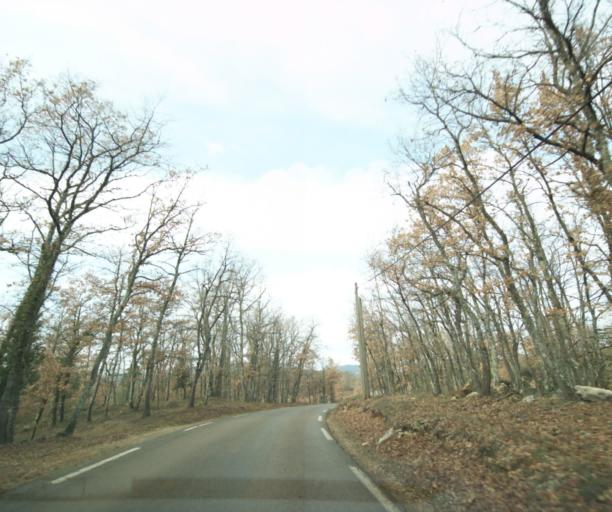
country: FR
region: Provence-Alpes-Cote d'Azur
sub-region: Departement du Var
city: Rougiers
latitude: 43.3937
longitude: 5.8874
